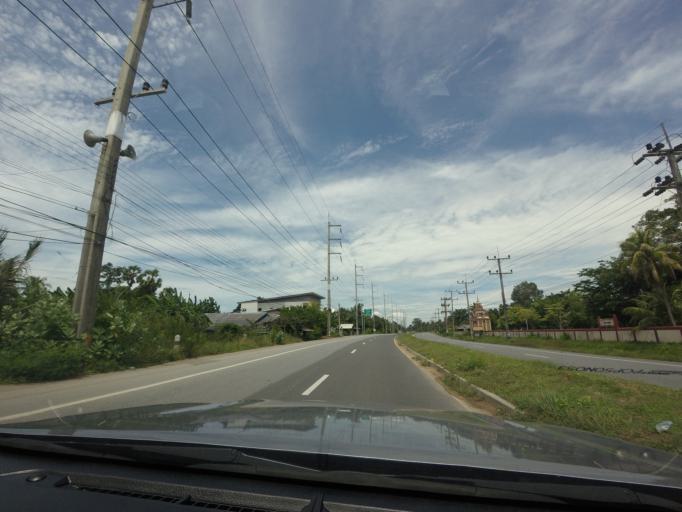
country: TH
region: Songkhla
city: Krasae Sin
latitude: 7.6182
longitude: 100.3973
